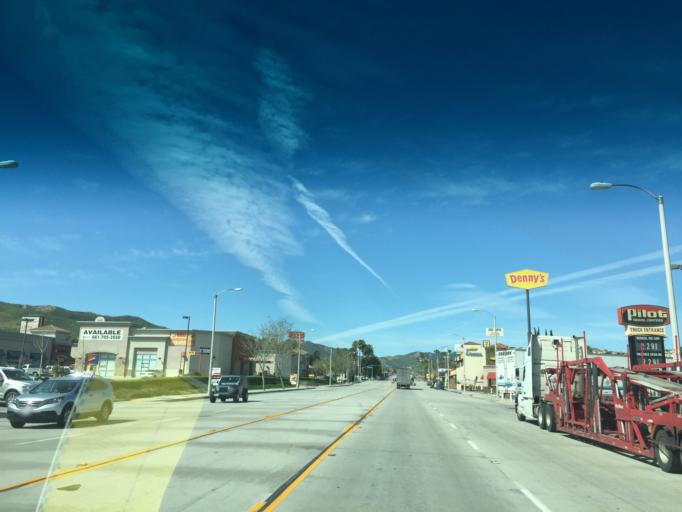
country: US
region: California
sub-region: Los Angeles County
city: Castaic
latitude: 34.4944
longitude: -118.6208
